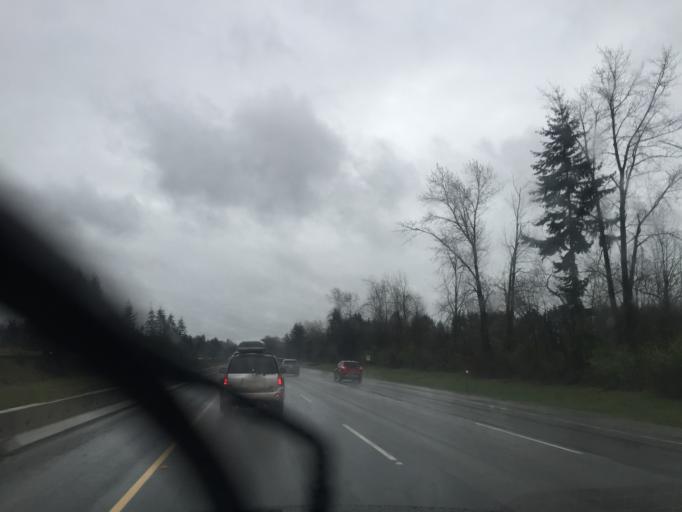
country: CA
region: British Columbia
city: Langley
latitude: 49.1267
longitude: -122.5572
